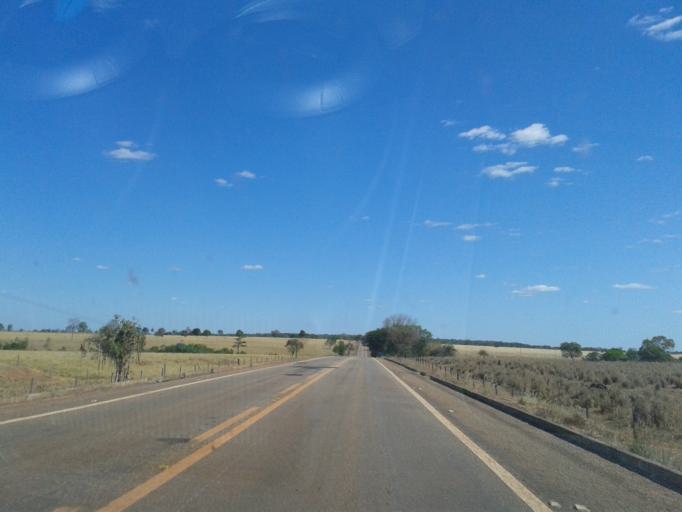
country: BR
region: Goias
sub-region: Sao Miguel Do Araguaia
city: Sao Miguel do Araguaia
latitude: -13.4446
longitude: -50.2917
